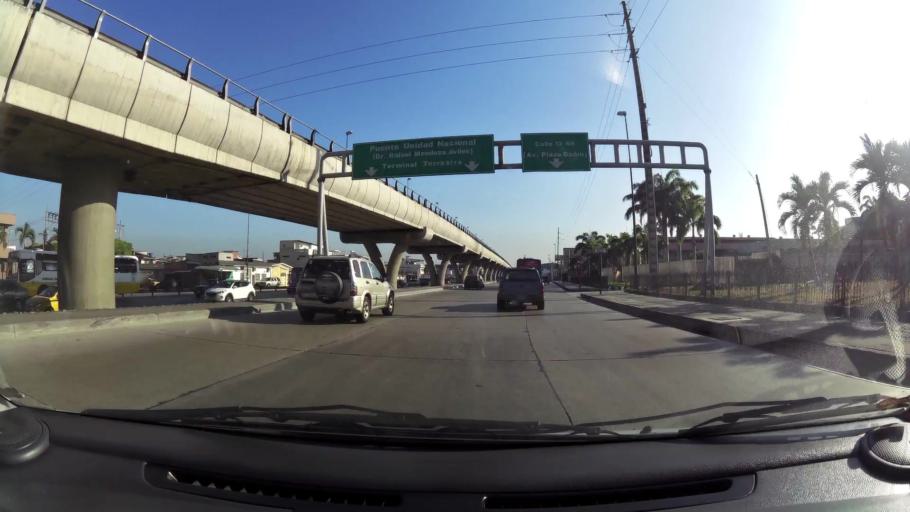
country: EC
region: Guayas
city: Eloy Alfaro
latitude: -2.1738
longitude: -79.8793
